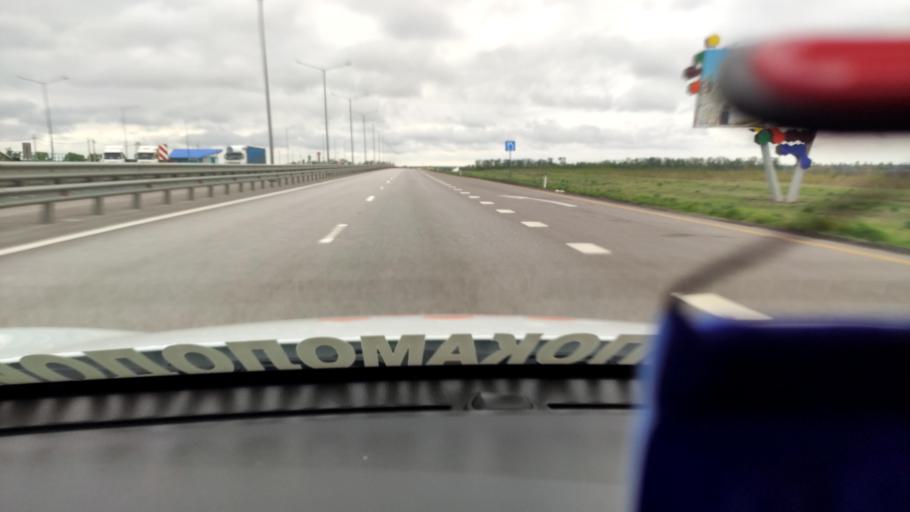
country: RU
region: Voronezj
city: Podkletnoye
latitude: 51.5417
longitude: 39.5006
